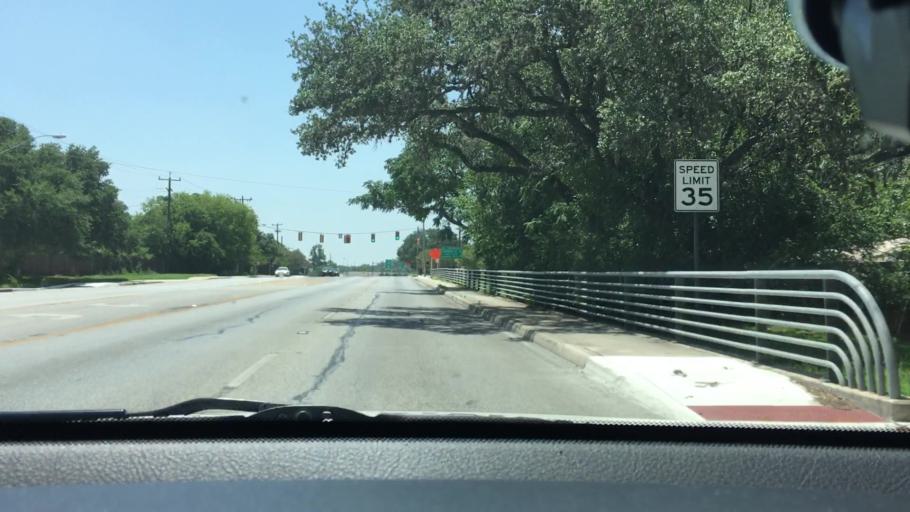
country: US
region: Texas
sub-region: Bexar County
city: Castle Hills
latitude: 29.5255
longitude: -98.5172
